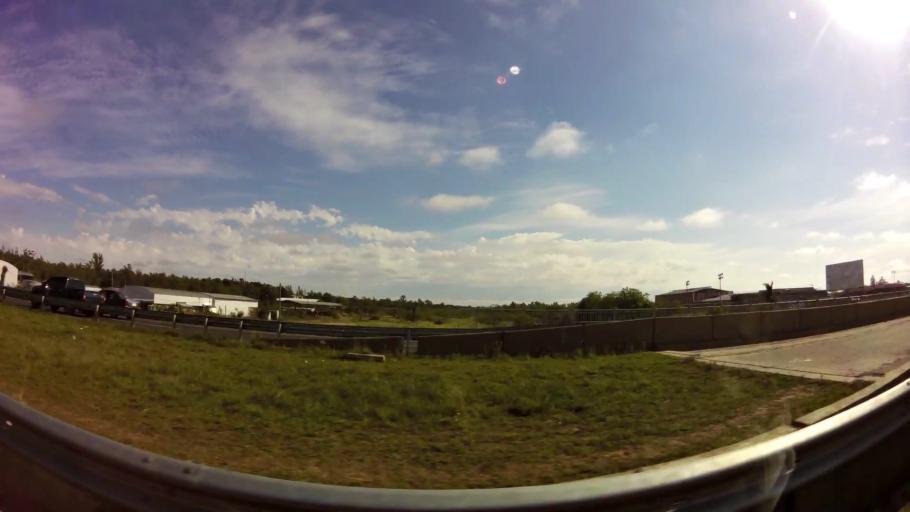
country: PY
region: Central
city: Fernando de la Mora
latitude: -25.2593
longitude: -57.5356
